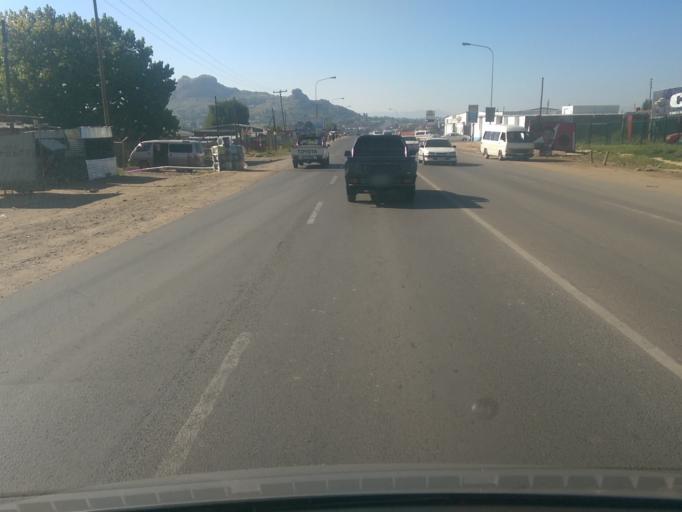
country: LS
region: Maseru
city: Maseru
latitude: -29.3359
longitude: 27.5101
